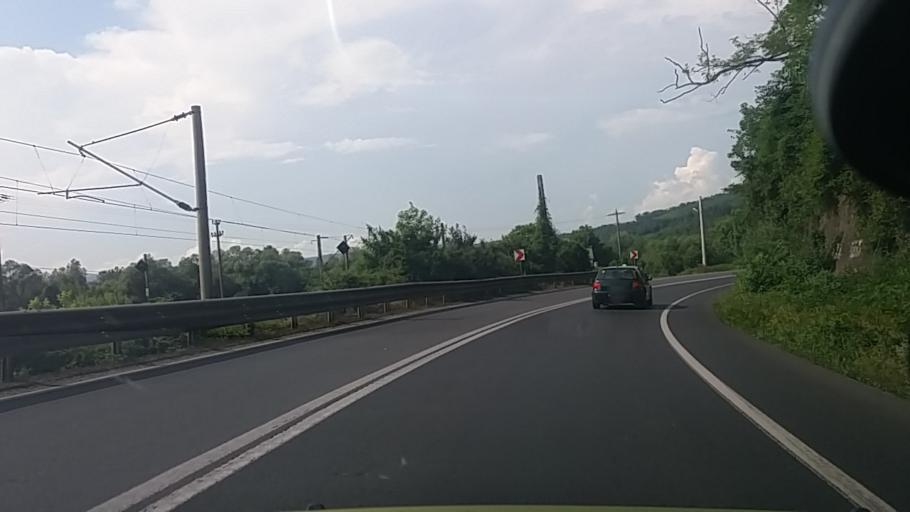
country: RO
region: Arad
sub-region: Comuna Barzava
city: Barzava
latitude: 46.0839
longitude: 22.0227
